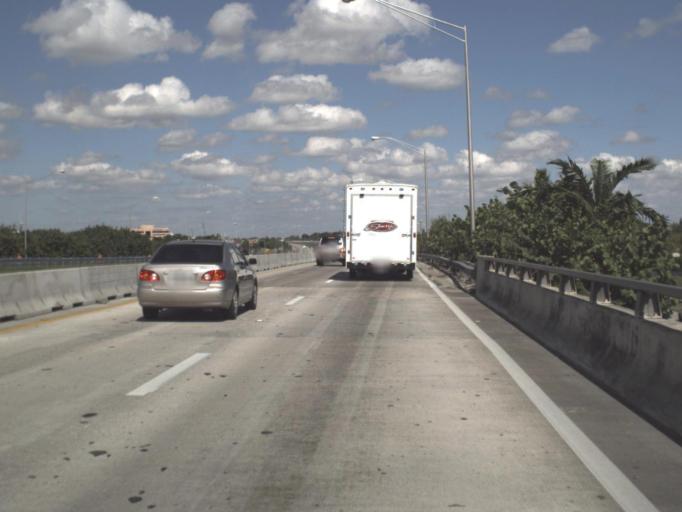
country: US
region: Florida
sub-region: Miami-Dade County
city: Goulds
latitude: 25.5665
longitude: -80.3628
